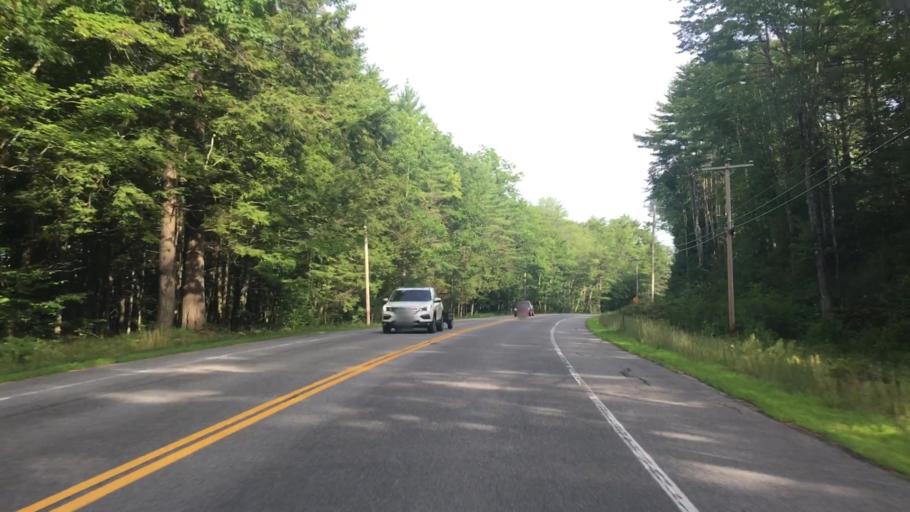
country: US
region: Maine
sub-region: York County
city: Limington
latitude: 43.7397
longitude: -70.6732
